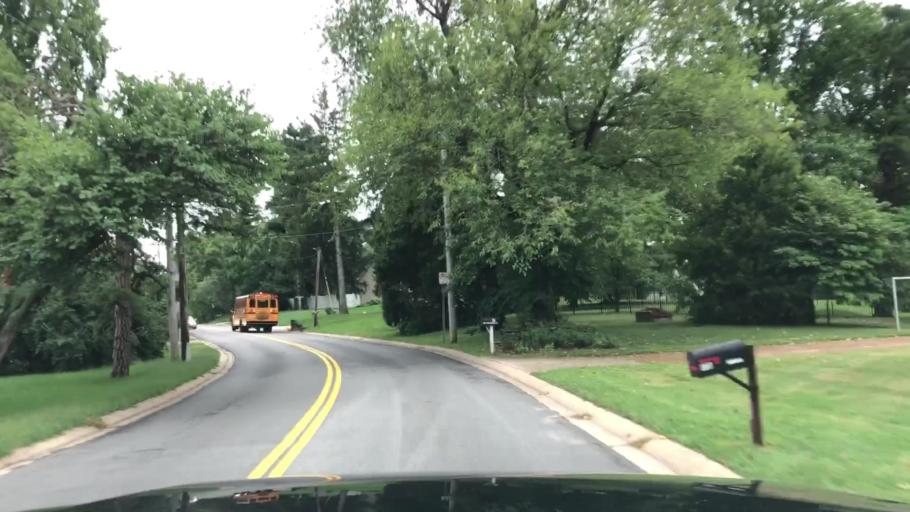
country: US
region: Missouri
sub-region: Saint Louis County
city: Manchester
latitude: 38.5857
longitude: -90.5101
